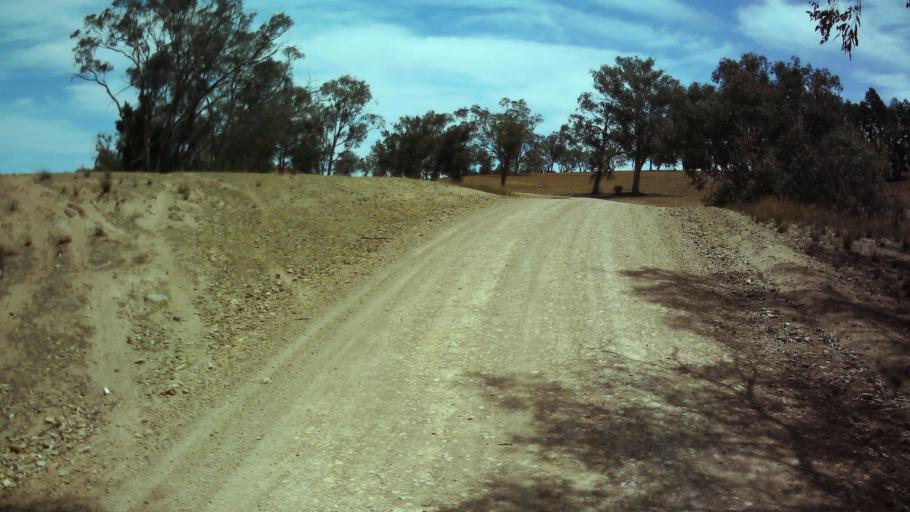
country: AU
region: New South Wales
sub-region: Weddin
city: Grenfell
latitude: -33.7442
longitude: 148.1736
